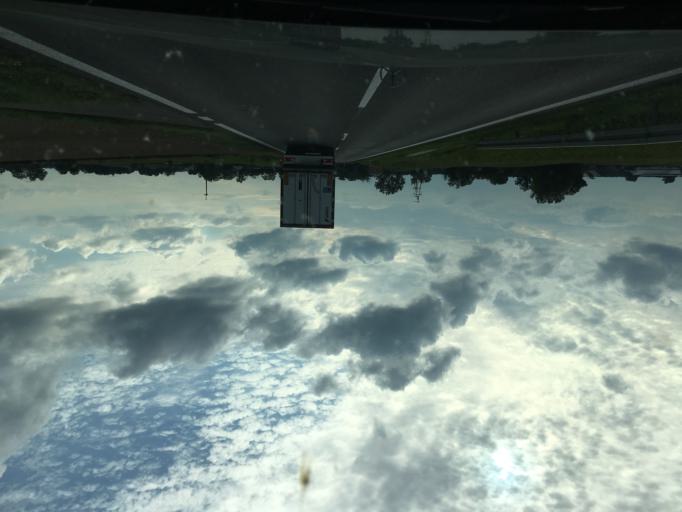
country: PL
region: Podlasie
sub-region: Powiat grajewski
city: Grajewo
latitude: 53.6693
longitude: 22.5563
